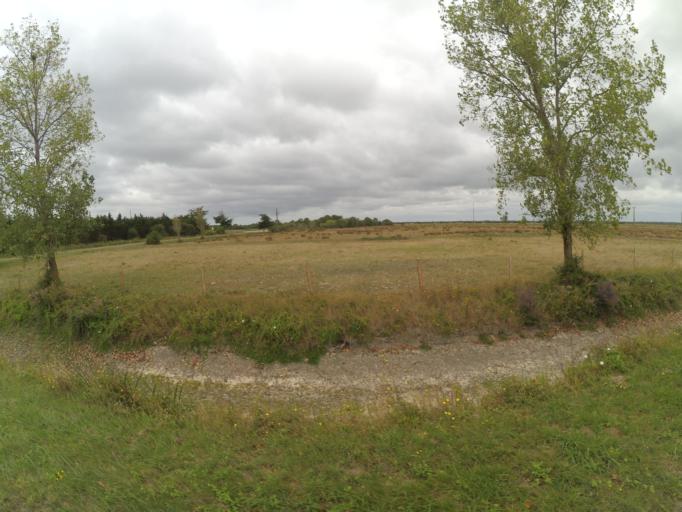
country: FR
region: Pays de la Loire
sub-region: Departement de la Vendee
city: Triaize
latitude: 46.4031
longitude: -1.2969
